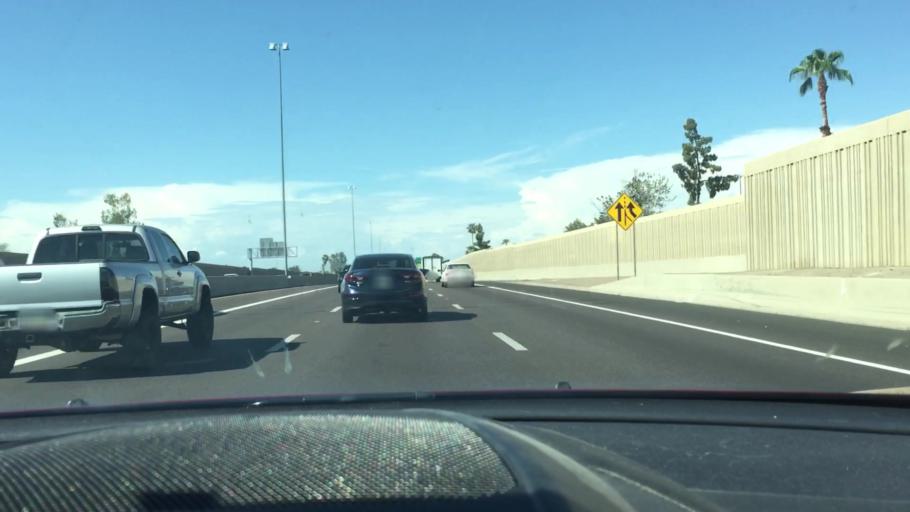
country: US
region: Arizona
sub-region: Maricopa County
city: Phoenix
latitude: 33.4830
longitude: -112.1123
